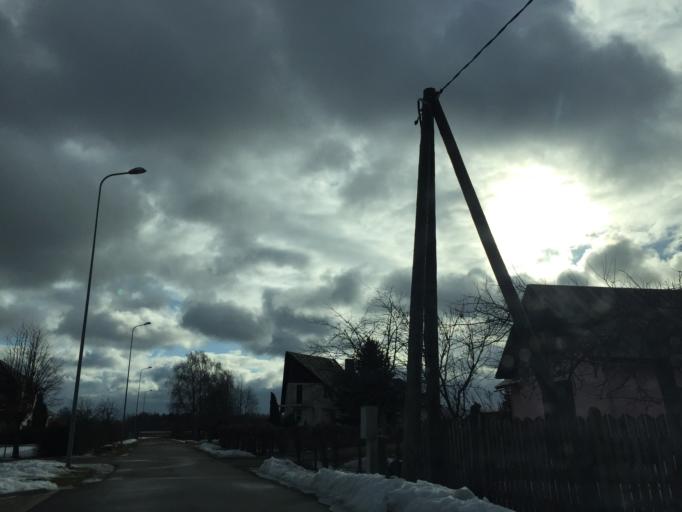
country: LV
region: Aloja
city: Aloja
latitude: 57.7709
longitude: 24.8187
